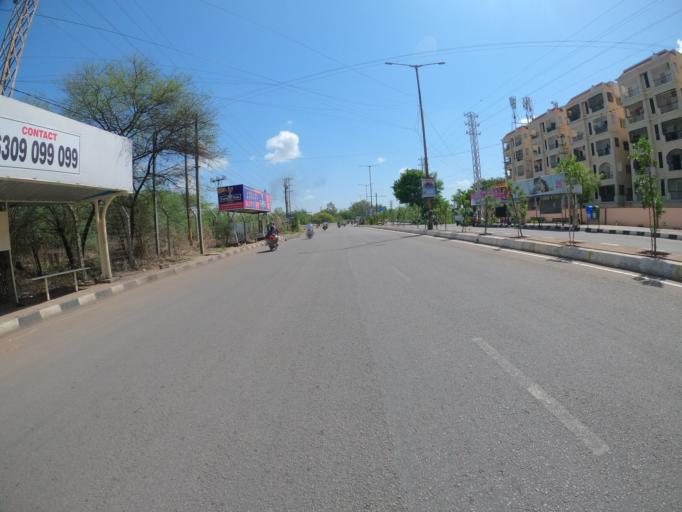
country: IN
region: Telangana
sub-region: Hyderabad
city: Hyderabad
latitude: 17.3709
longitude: 78.4044
